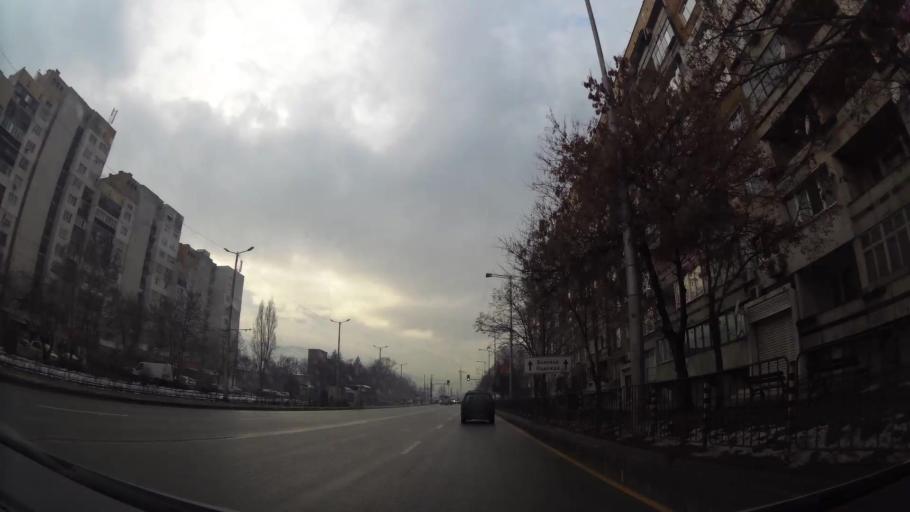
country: BG
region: Sofia-Capital
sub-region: Stolichna Obshtina
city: Sofia
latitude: 42.6938
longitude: 23.2825
